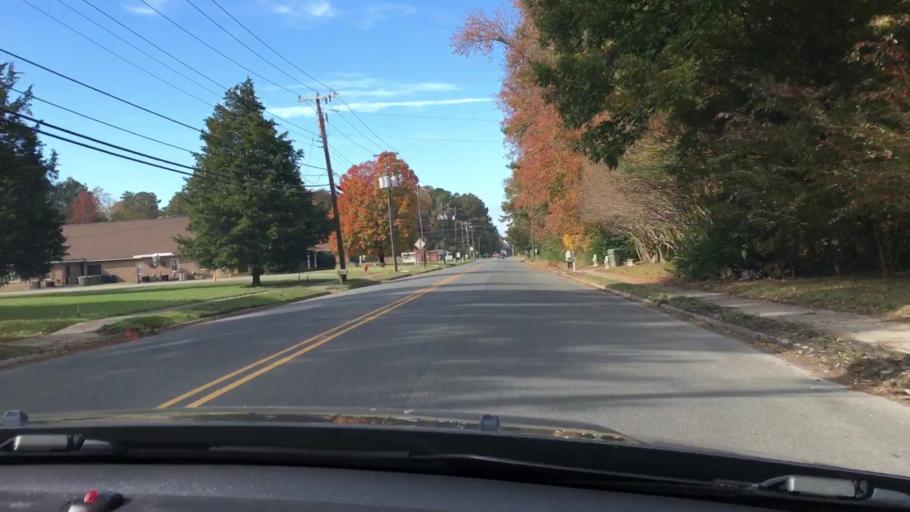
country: US
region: Virginia
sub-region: King William County
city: West Point
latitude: 37.5558
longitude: -76.8162
